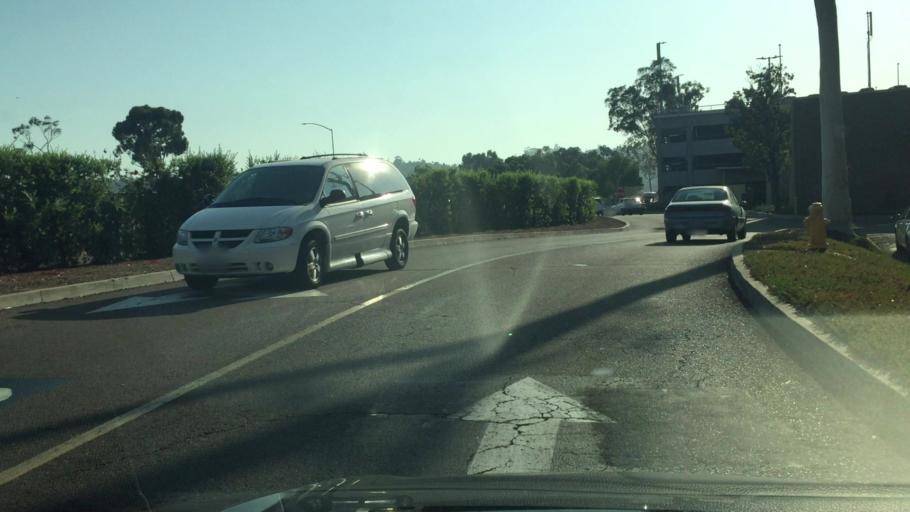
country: US
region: California
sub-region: San Diego County
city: El Cajon
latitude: 32.8040
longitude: -116.9655
